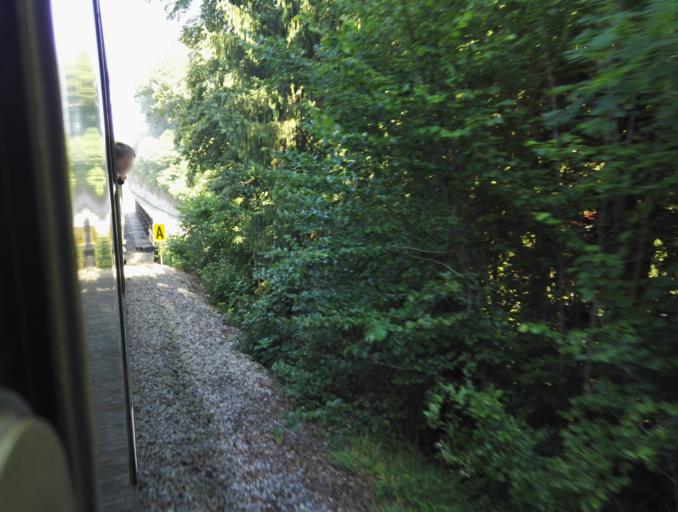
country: DE
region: Baden-Wuerttemberg
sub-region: Regierungsbezirk Stuttgart
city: Welzheim
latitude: 48.8816
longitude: 9.6063
